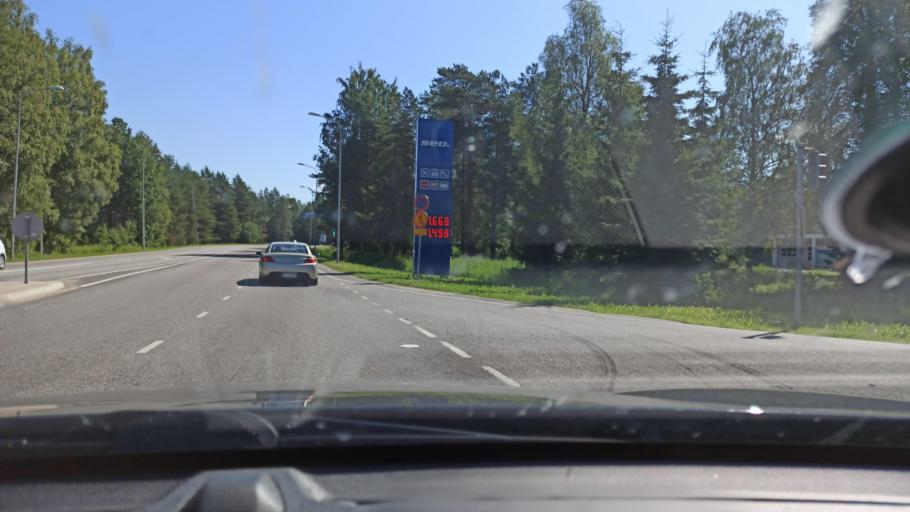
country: FI
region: Northern Ostrobothnia
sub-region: Oulu
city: Oulu
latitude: 65.0393
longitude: 25.4656
